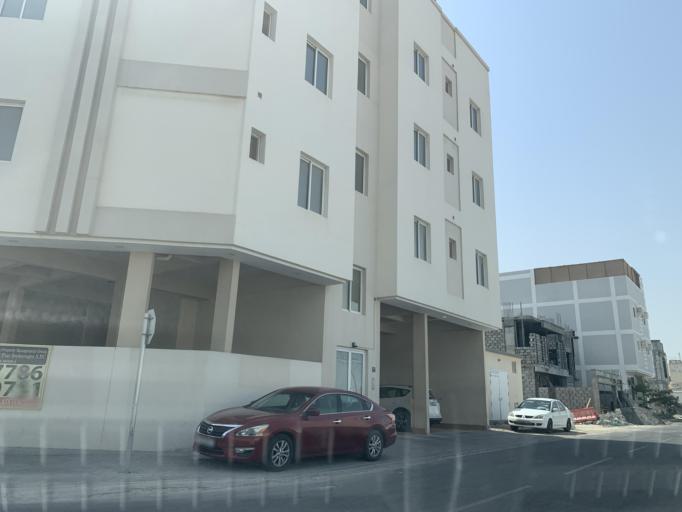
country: BH
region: Northern
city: Madinat `Isa
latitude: 26.1870
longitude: 50.5430
